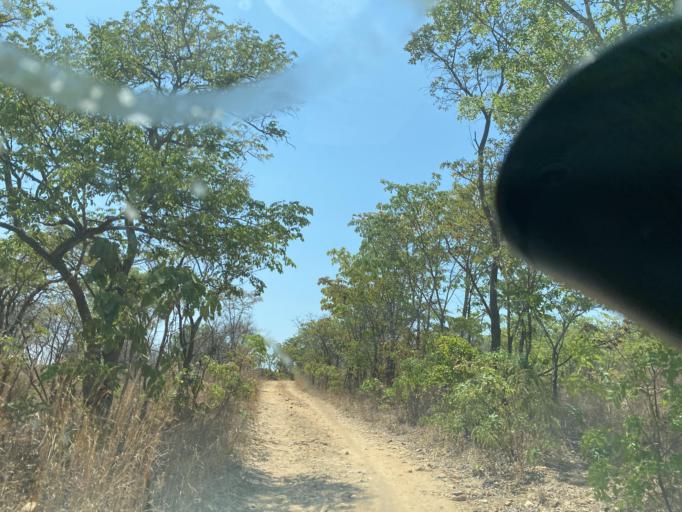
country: ZM
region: Lusaka
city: Chongwe
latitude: -15.4366
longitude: 29.1980
